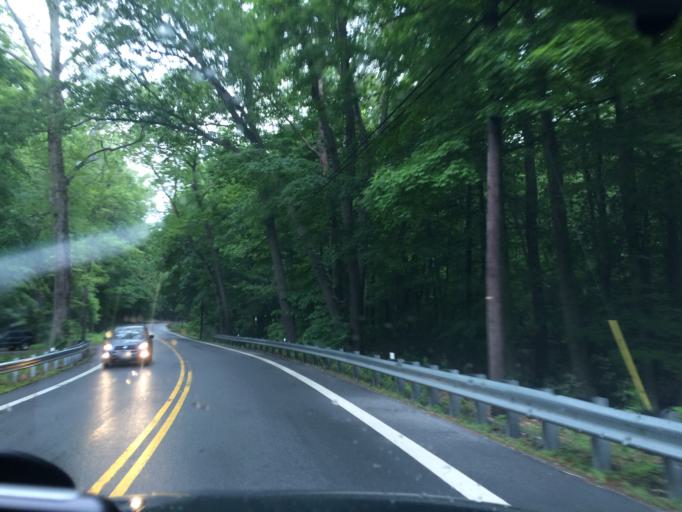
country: US
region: Maryland
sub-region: Frederick County
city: Thurmont
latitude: 39.6457
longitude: -77.4165
